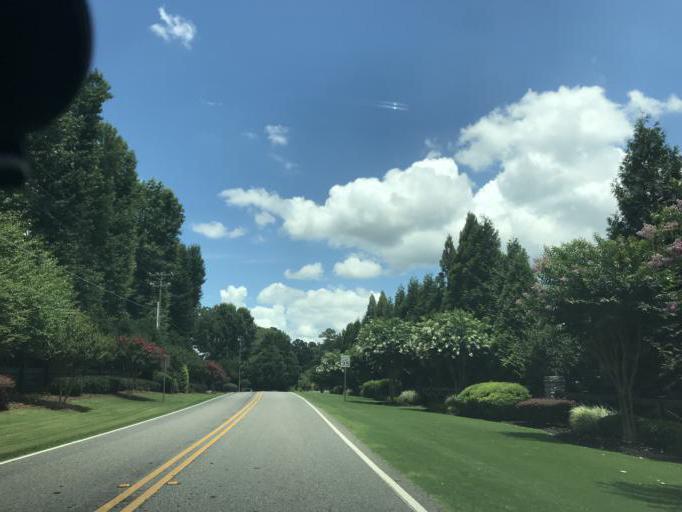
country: US
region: Georgia
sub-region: Fulton County
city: Johns Creek
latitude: 34.1091
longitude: -84.1673
